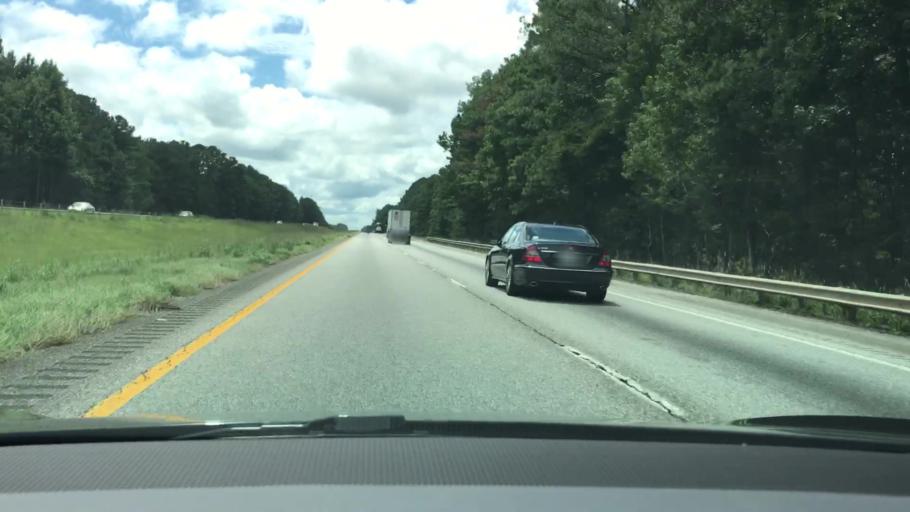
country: US
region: Alabama
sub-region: Chambers County
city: Huguley
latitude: 32.7691
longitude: -85.2603
